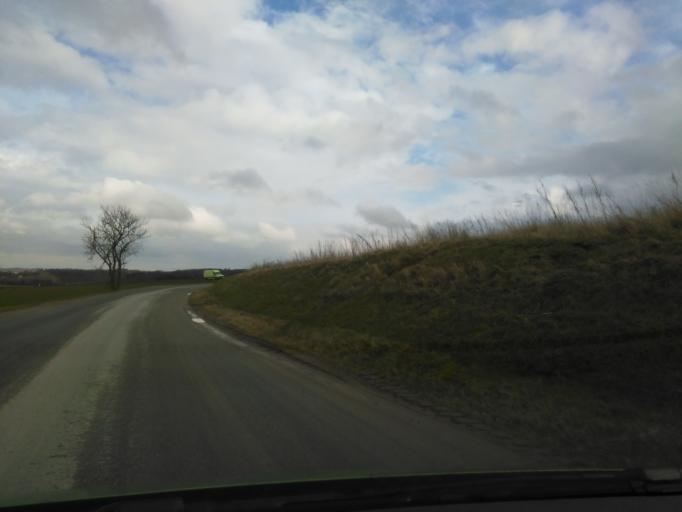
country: DK
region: Central Jutland
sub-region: Skanderborg Kommune
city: Skovby
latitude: 56.1092
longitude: 9.9753
